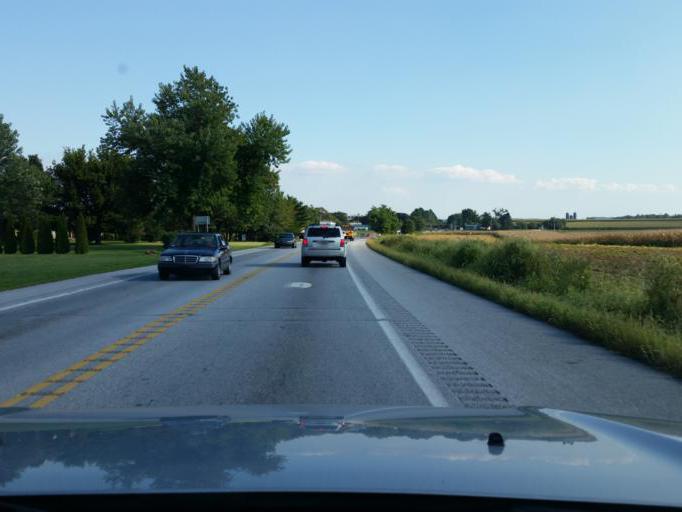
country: US
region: Pennsylvania
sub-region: Chester County
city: Atglen
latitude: 39.9330
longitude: -75.9533
